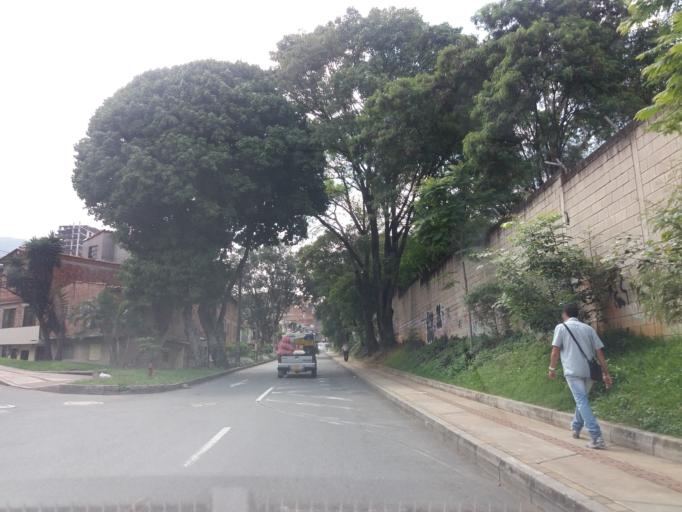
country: CO
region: Antioquia
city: Medellin
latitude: 6.2849
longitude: -75.5627
